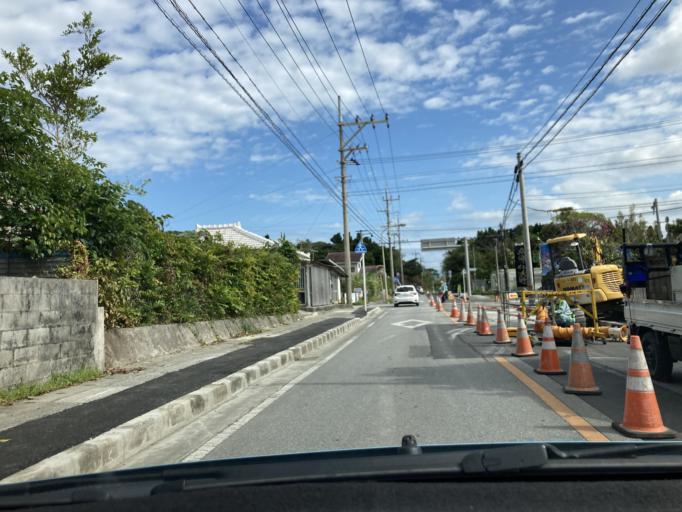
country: JP
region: Okinawa
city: Nago
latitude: 26.7004
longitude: 127.9285
